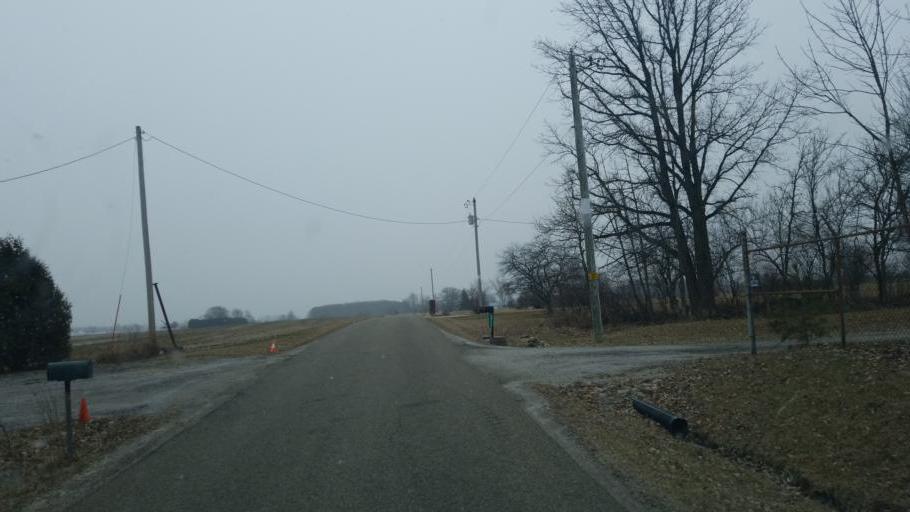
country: US
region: Ohio
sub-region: Defiance County
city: Hicksville
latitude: 41.3316
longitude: -84.7382
